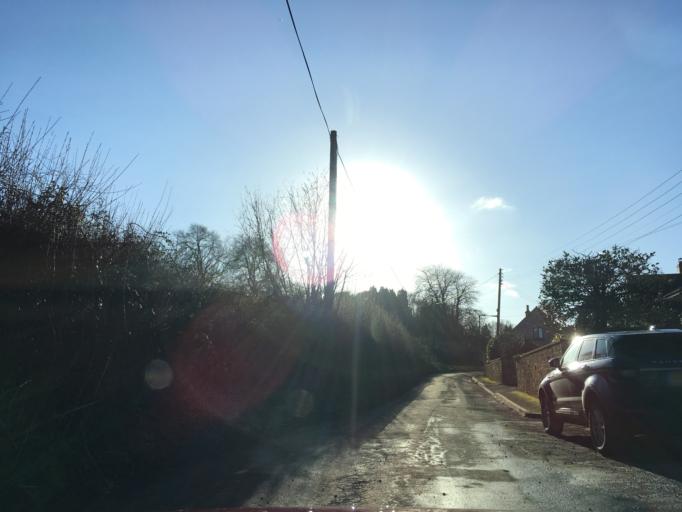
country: GB
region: England
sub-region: South Gloucestershire
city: Horton
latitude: 51.5336
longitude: -2.3523
